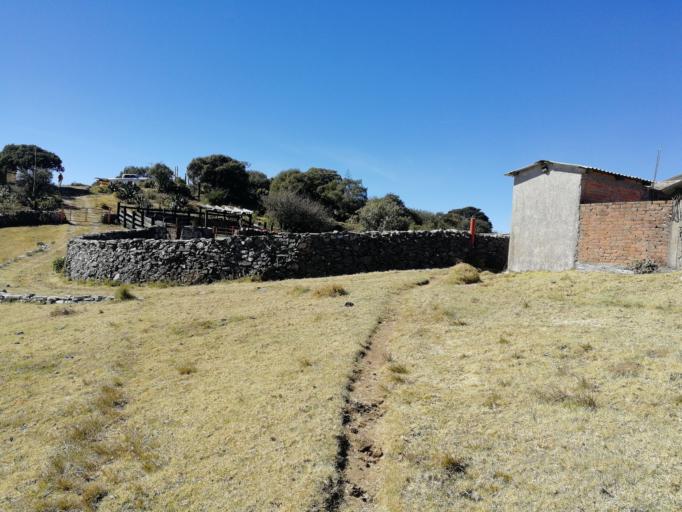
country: MX
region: San Luis Potosi
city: Zaragoza
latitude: 22.0103
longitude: -100.6195
